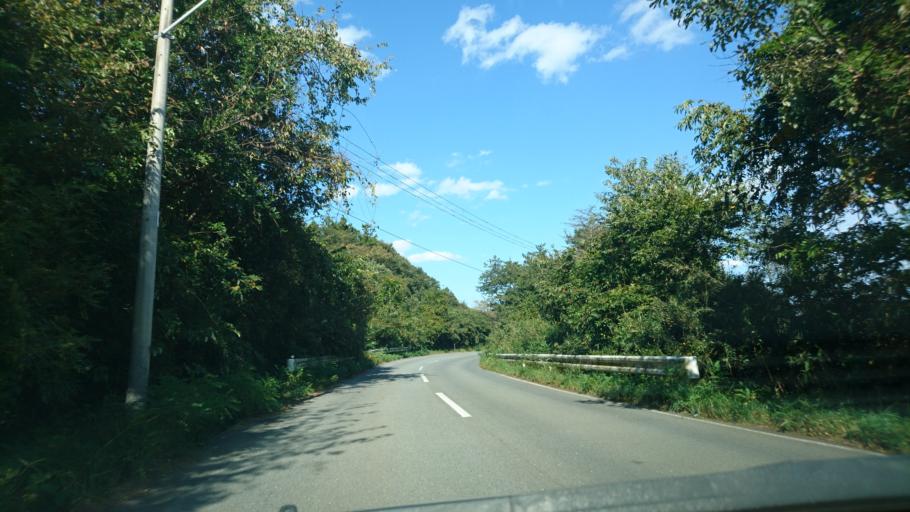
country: JP
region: Iwate
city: Ichinoseki
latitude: 38.8529
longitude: 141.0475
